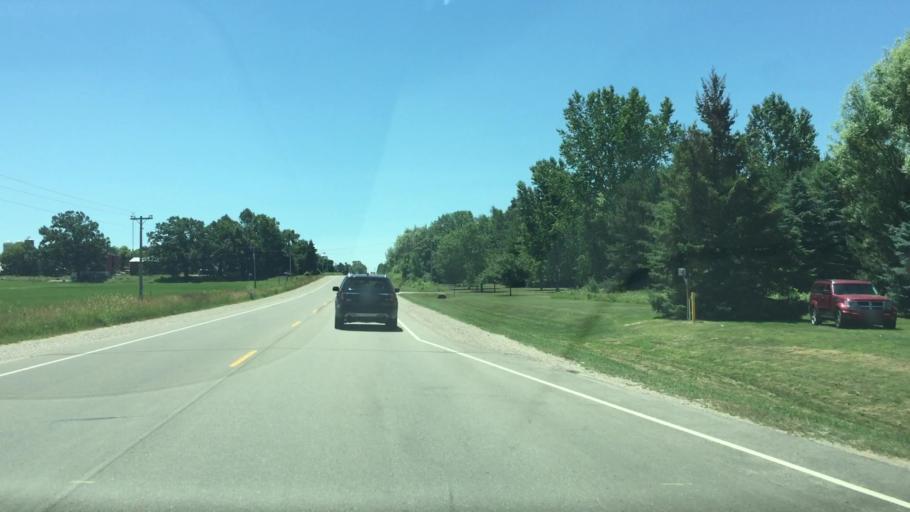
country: US
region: Wisconsin
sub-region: Calumet County
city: New Holstein
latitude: 43.9713
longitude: -88.1124
